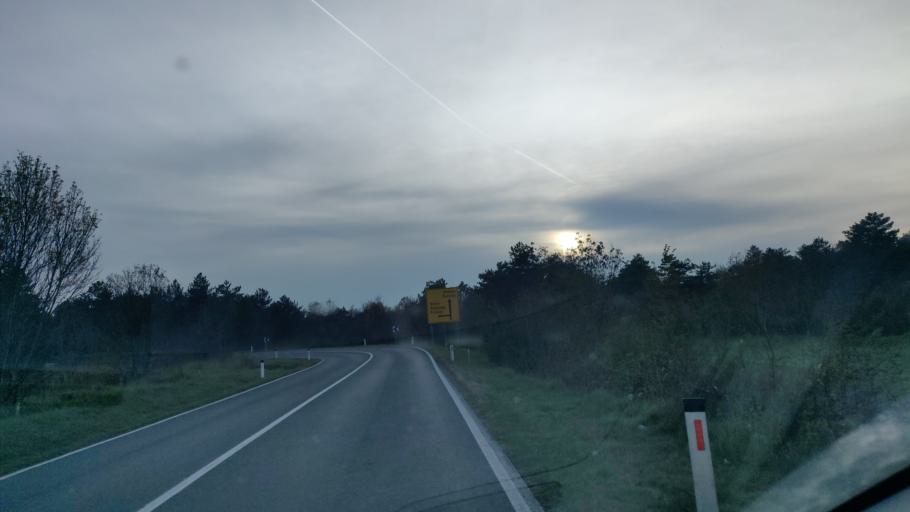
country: IT
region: Friuli Venezia Giulia
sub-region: Provincia di Trieste
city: Zolla
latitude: 45.8070
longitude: 13.8448
